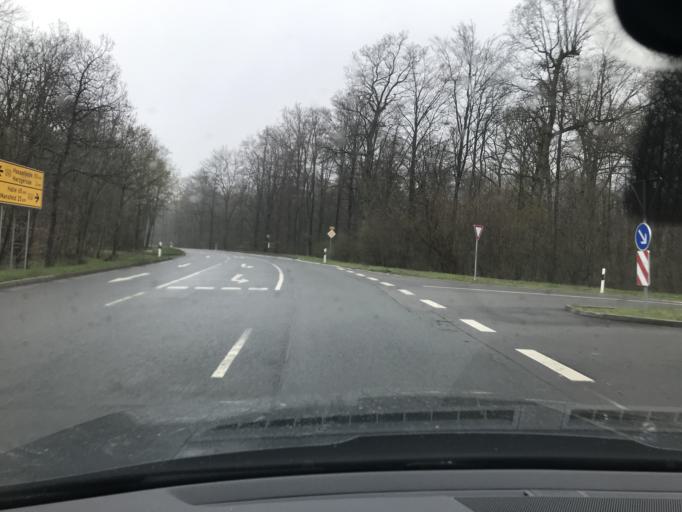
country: DE
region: Saxony-Anhalt
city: Harzgerode
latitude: 51.6228
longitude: 11.1508
